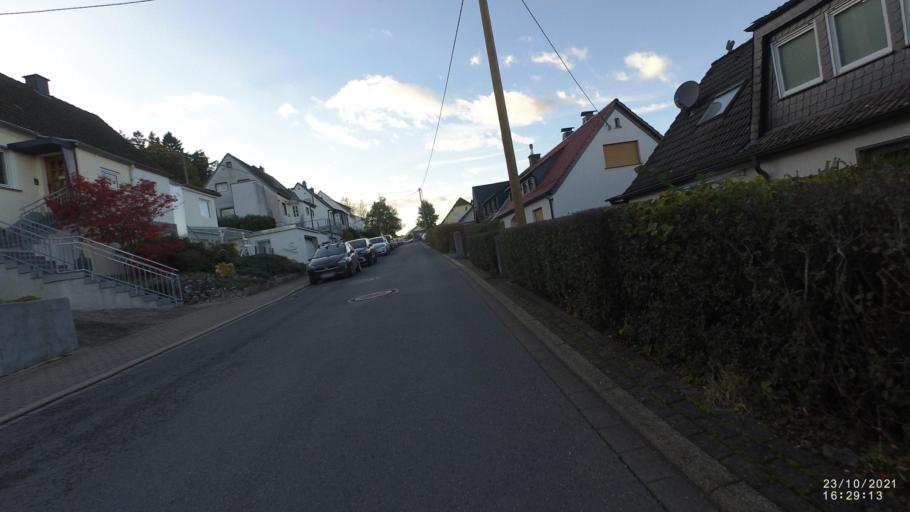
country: DE
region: North Rhine-Westphalia
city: Hemer
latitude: 51.3784
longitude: 7.8156
